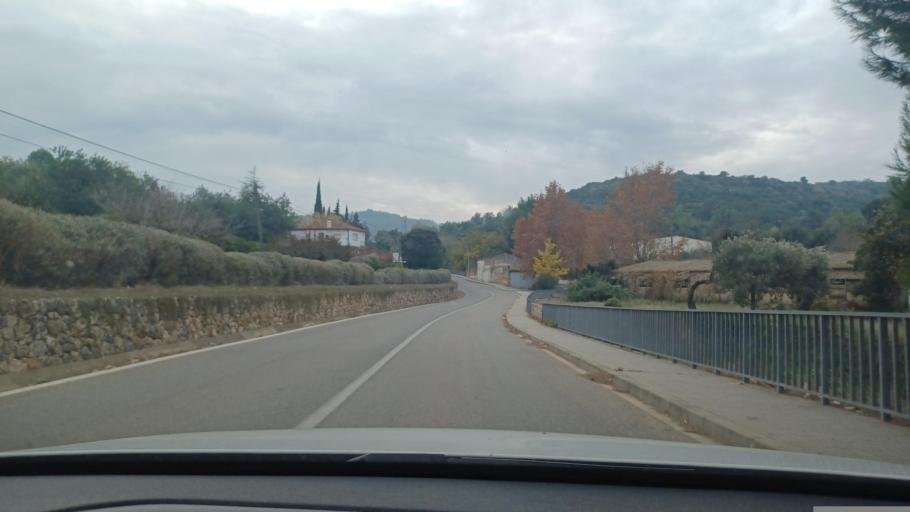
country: ES
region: Catalonia
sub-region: Provincia de Tarragona
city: Santa Barbara
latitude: 40.6601
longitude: 0.4654
